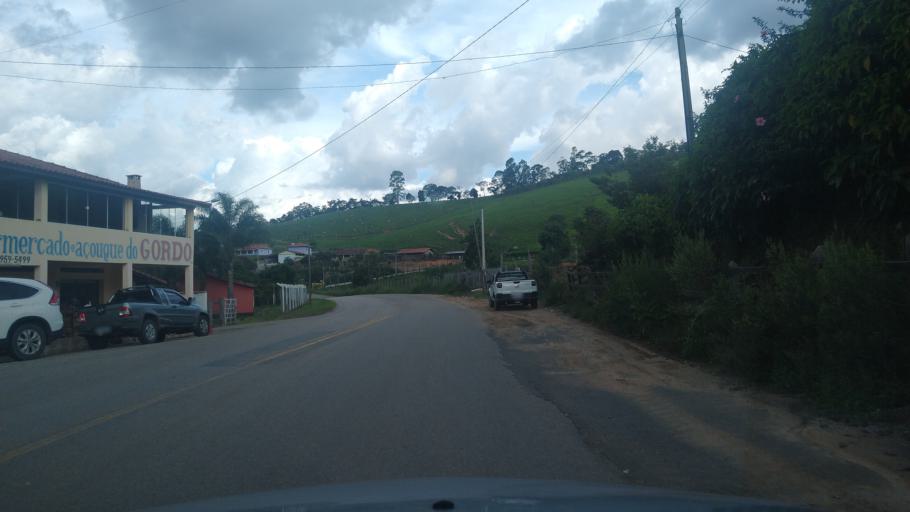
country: BR
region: Minas Gerais
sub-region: Extrema
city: Extrema
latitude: -22.7609
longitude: -46.3352
